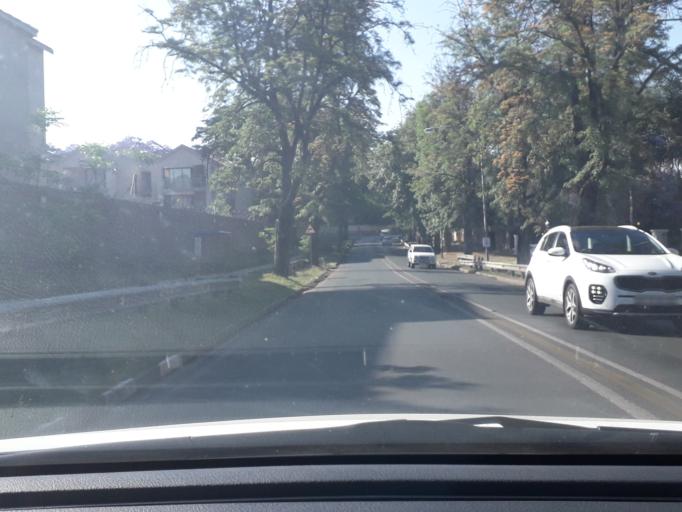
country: ZA
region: Gauteng
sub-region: City of Johannesburg Metropolitan Municipality
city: Johannesburg
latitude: -26.1583
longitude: 28.0344
